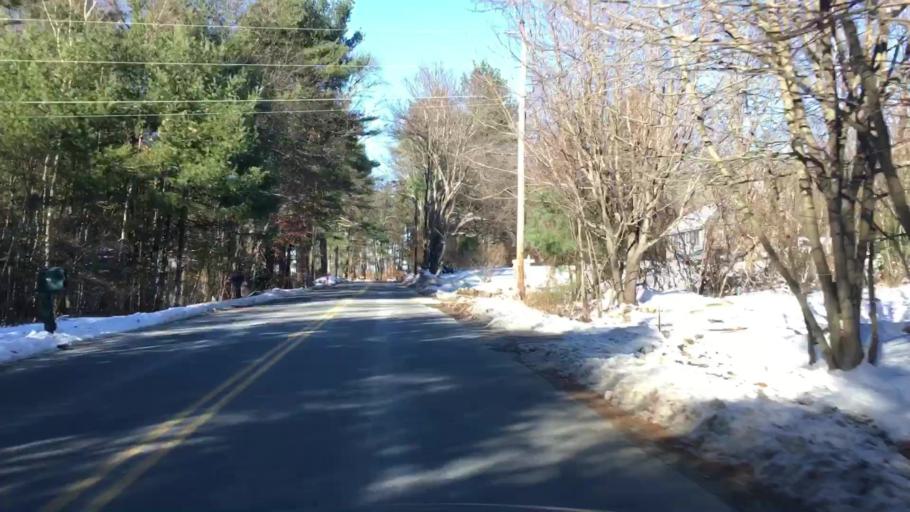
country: US
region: New Hampshire
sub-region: Hillsborough County
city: Milford
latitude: 42.8183
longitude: -71.6331
